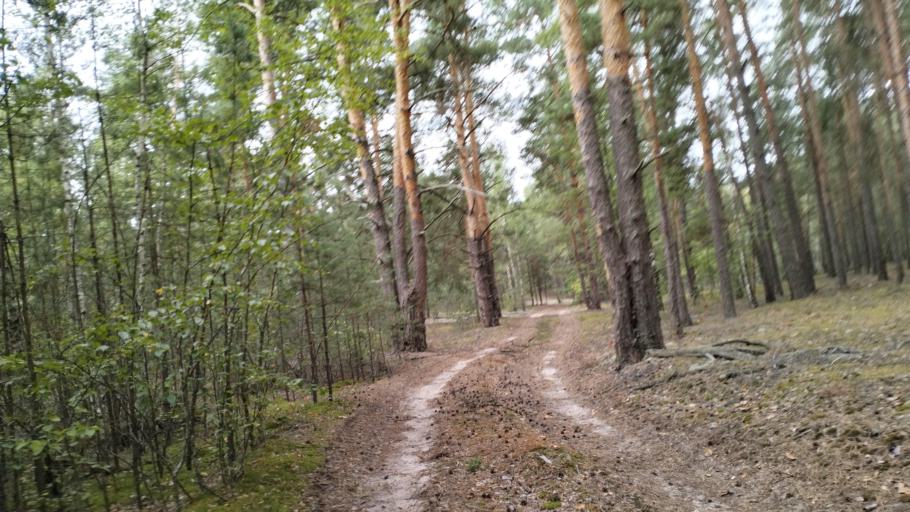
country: BY
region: Brest
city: Davyd-Haradok
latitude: 51.8789
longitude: 27.2198
